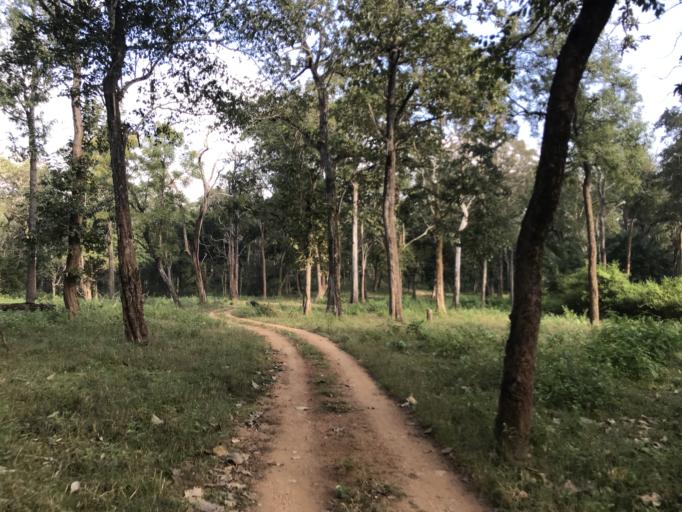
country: IN
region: Karnataka
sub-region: Mysore
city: Heggadadevankote
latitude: 11.9481
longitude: 76.1940
